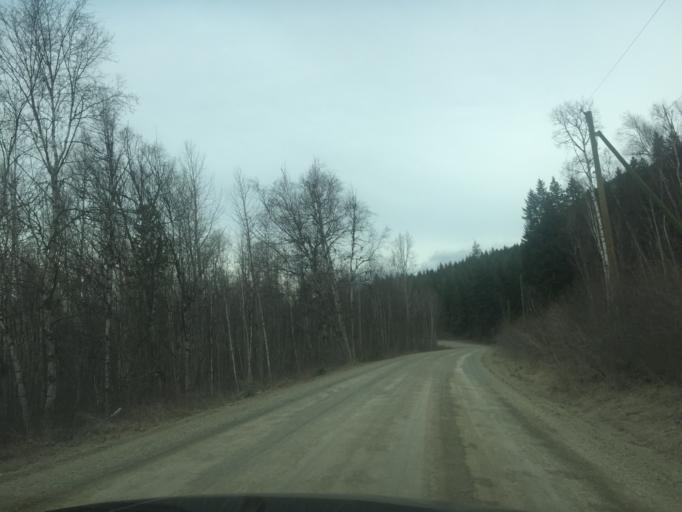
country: CA
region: British Columbia
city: Kamloops
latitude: 51.2865
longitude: -120.1505
